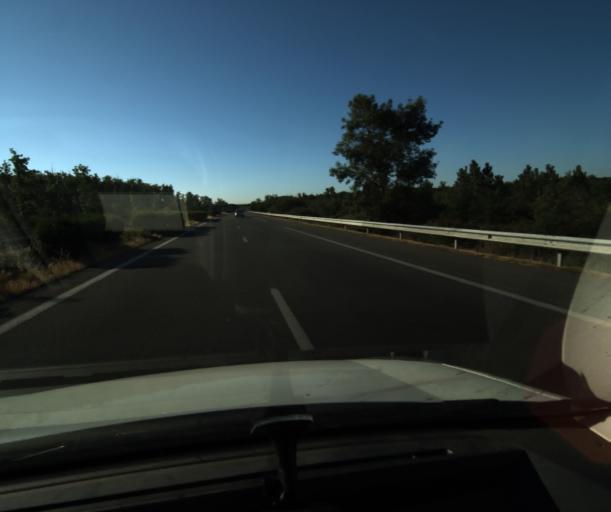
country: FR
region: Midi-Pyrenees
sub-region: Departement du Tarn-et-Garonne
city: Saint-Porquier
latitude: 44.0022
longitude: 1.2240
